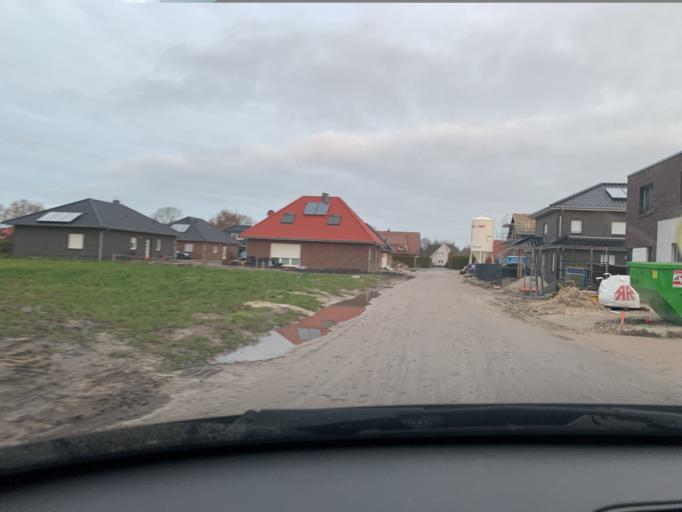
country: DE
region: Lower Saxony
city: Westerstede
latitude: 53.2516
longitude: 7.9039
